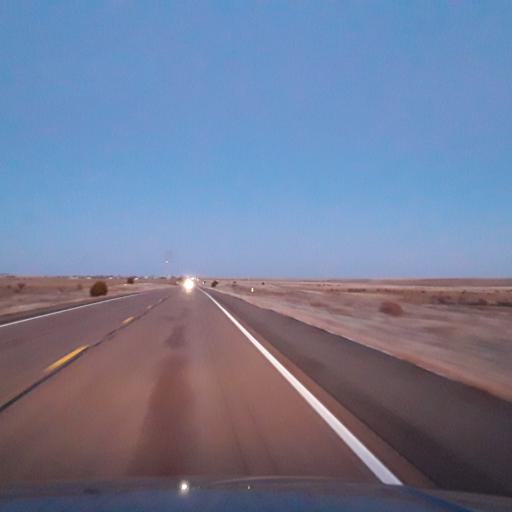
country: US
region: New Mexico
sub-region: Guadalupe County
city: Santa Rosa
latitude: 34.7702
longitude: -104.9668
